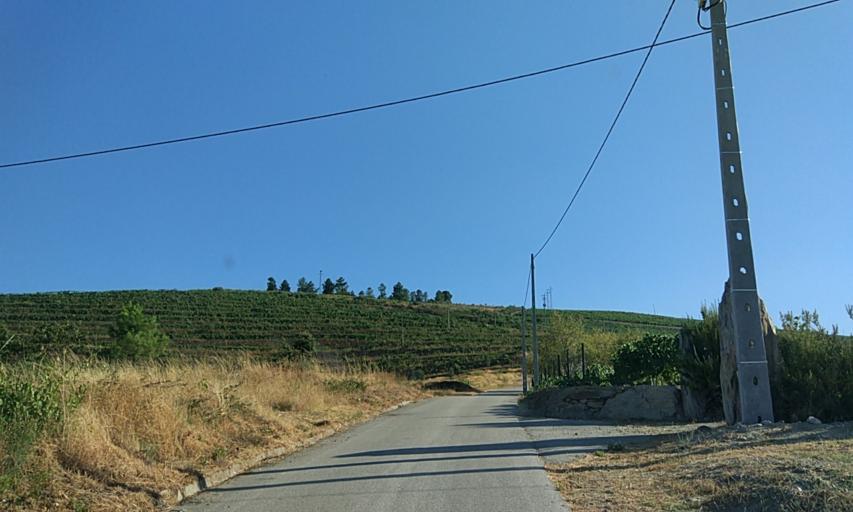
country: PT
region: Viseu
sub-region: Sao Joao da Pesqueira
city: Sao Joao da Pesqueira
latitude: 41.1693
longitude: -7.4090
